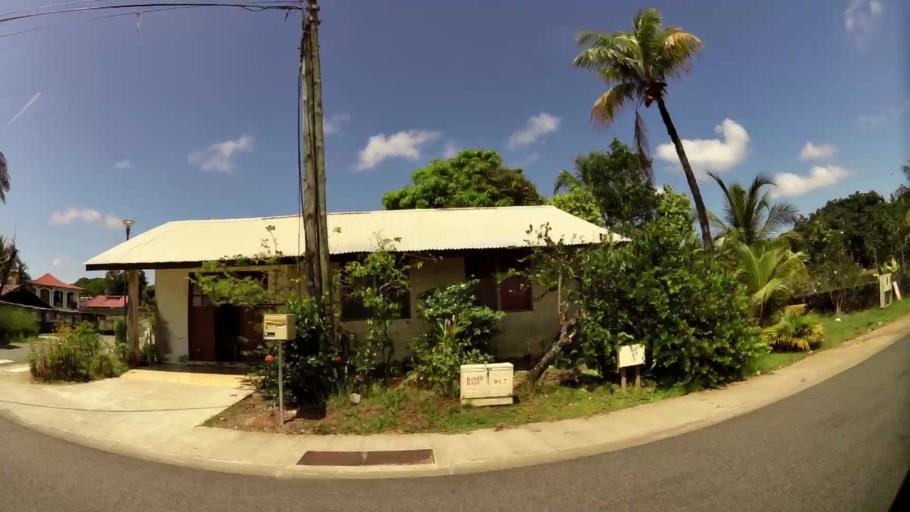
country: GF
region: Guyane
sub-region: Guyane
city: Cayenne
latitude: 4.9139
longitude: -52.3202
